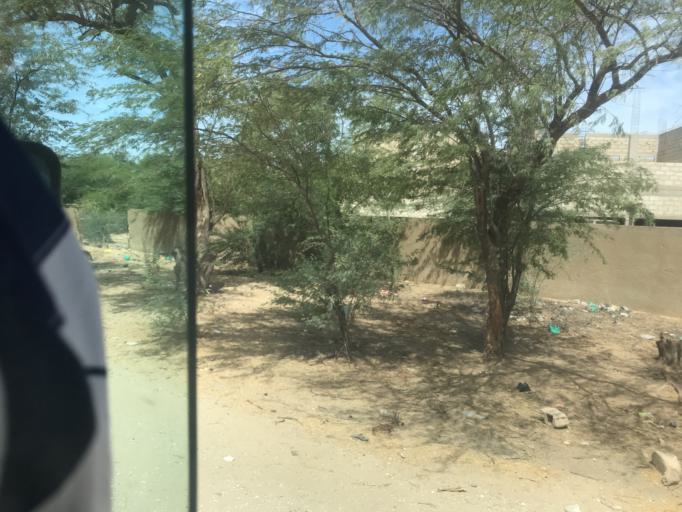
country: SN
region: Saint-Louis
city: Saint-Louis
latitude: 16.0560
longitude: -16.4260
